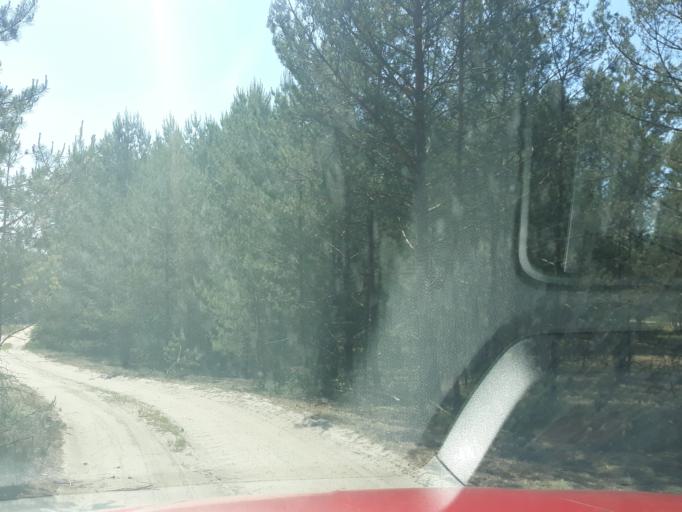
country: PL
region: Pomeranian Voivodeship
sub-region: Powiat chojnicki
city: Chojnice
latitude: 53.8719
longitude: 17.5396
